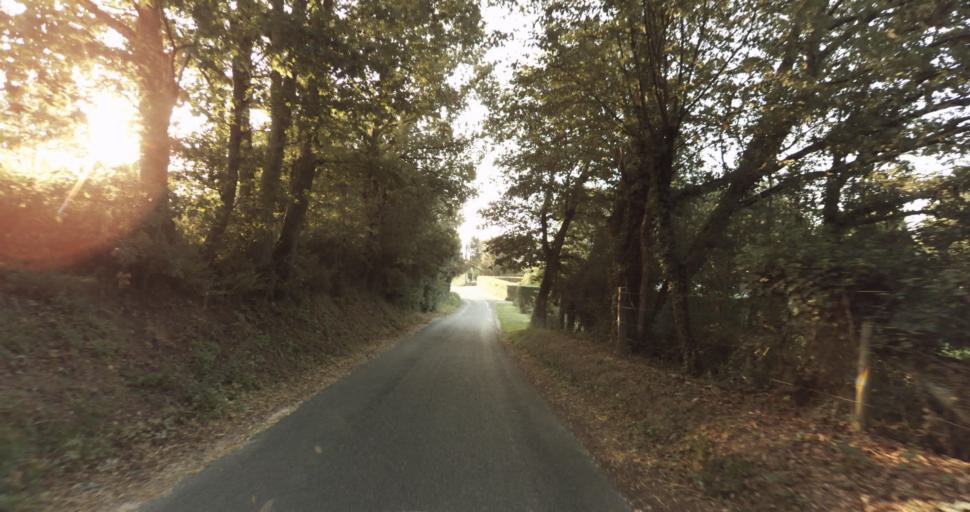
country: FR
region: Centre
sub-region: Departement d'Eure-et-Loir
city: Vert-en-Drouais
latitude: 48.7803
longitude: 1.3159
